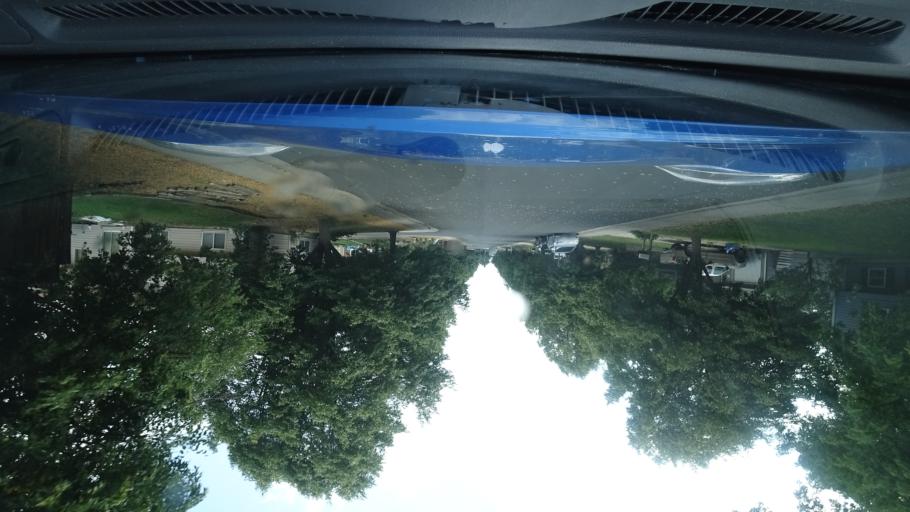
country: US
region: Colorado
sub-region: Adams County
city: Aurora
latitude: 39.6938
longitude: -104.7676
